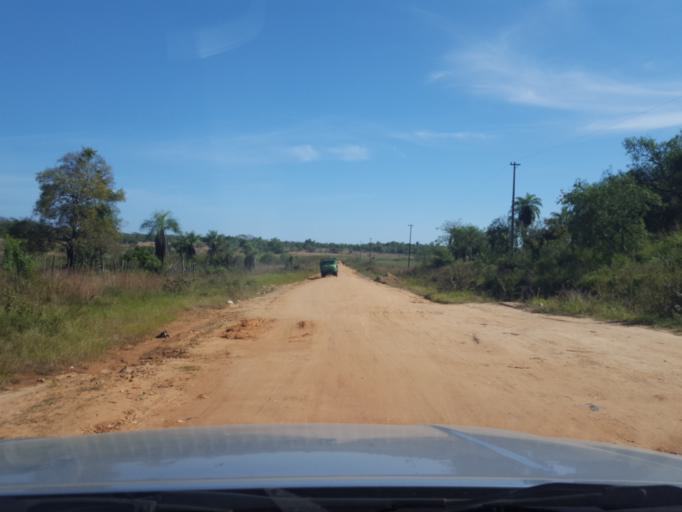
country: PY
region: Cordillera
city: Tobati
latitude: -25.2570
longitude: -57.0966
